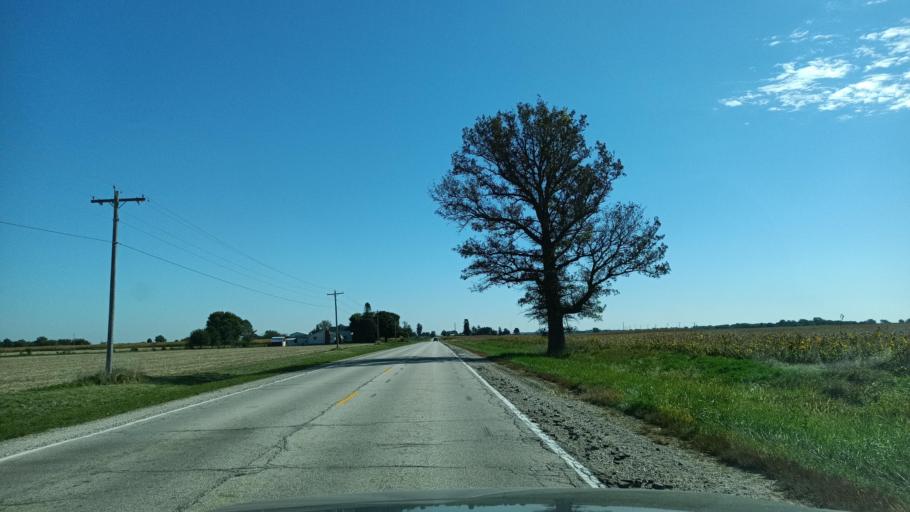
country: US
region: Illinois
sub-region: Knox County
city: Knoxville
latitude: 40.9083
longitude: -90.2314
